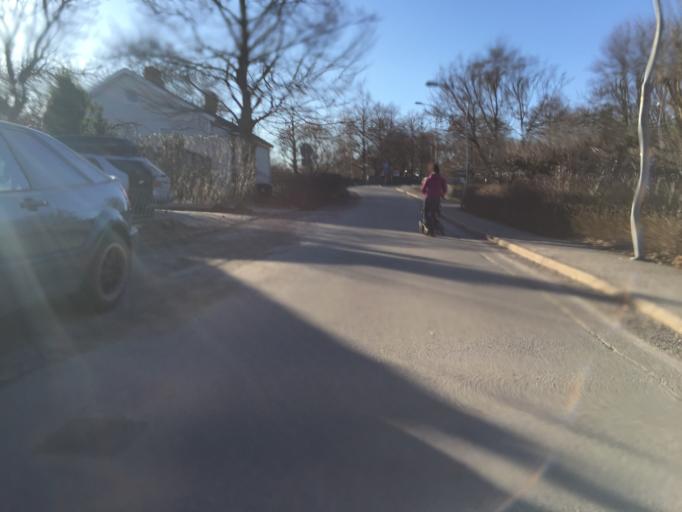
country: SE
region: Stockholm
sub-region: Stockholms Kommun
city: Bromma
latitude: 59.3548
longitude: 17.9252
